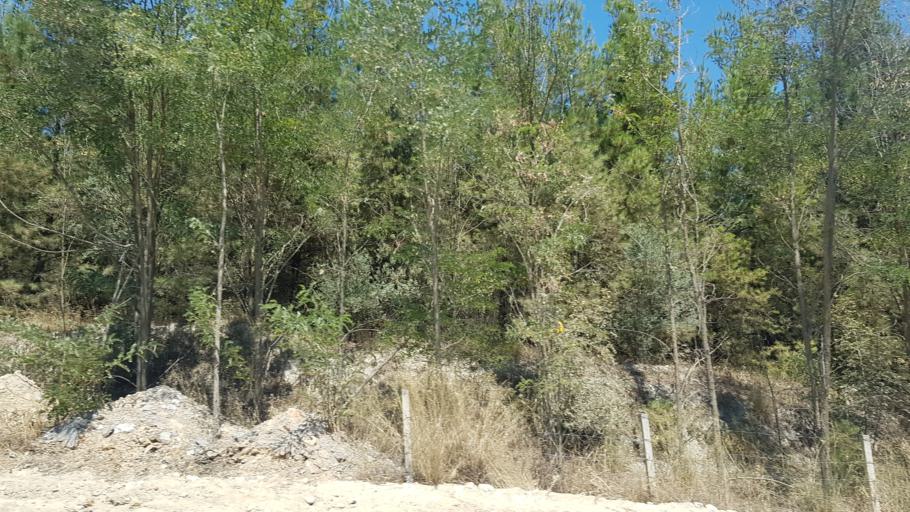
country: TR
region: Mugla
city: Yatagan
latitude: 37.3186
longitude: 28.0875
